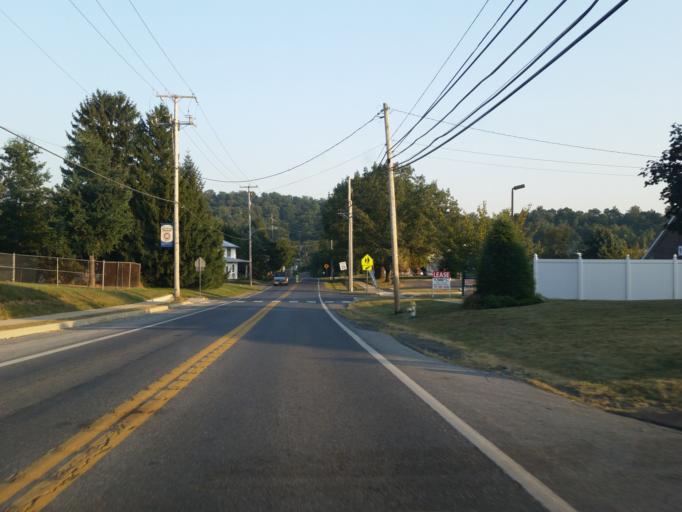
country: US
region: Pennsylvania
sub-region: Lebanon County
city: Jonestown
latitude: 40.4111
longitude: -76.4776
